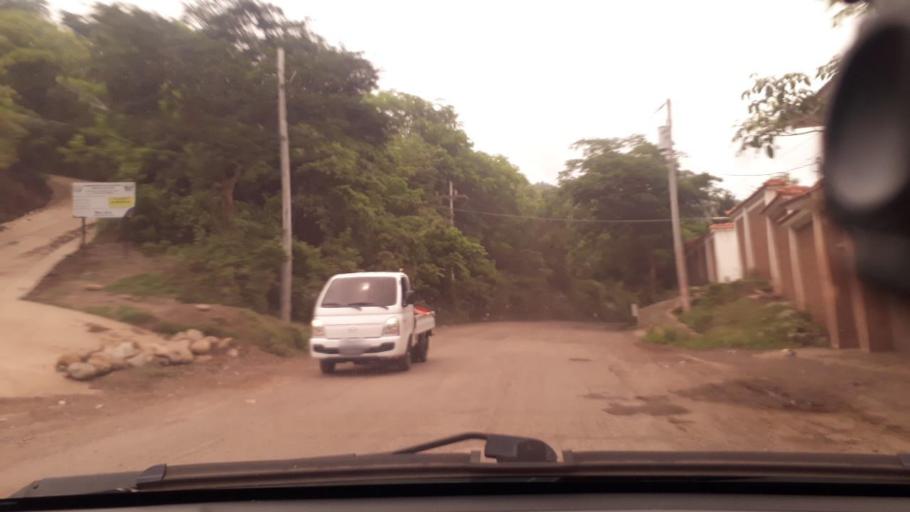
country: GT
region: Chiquimula
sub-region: Municipio de San Juan Ermita
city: San Juan Ermita
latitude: 14.7738
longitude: -89.4210
